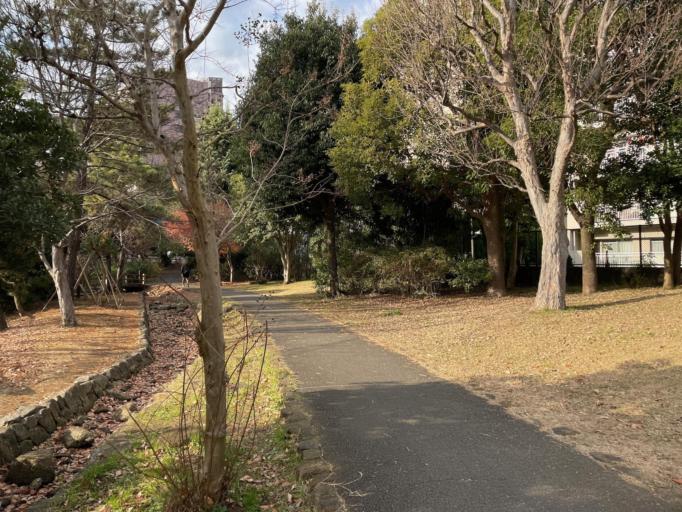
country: JP
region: Tokyo
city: Urayasu
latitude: 35.6754
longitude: 139.8276
